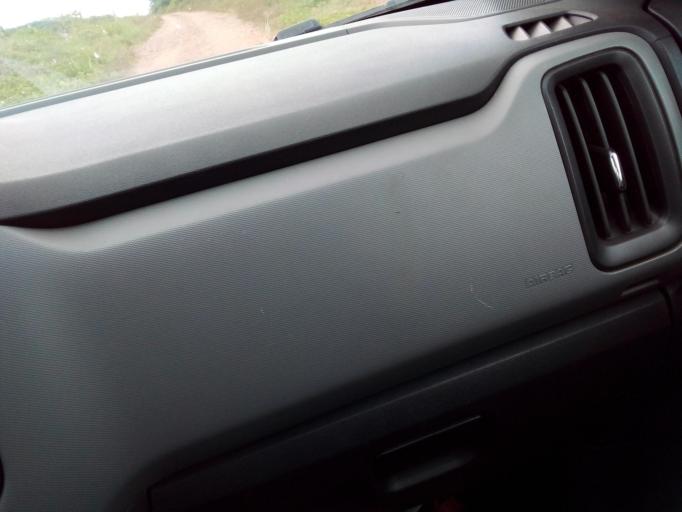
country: BR
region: Maranhao
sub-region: Itapecuru Mirim
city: Itapecuru Mirim
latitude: -3.0419
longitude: -44.3460
